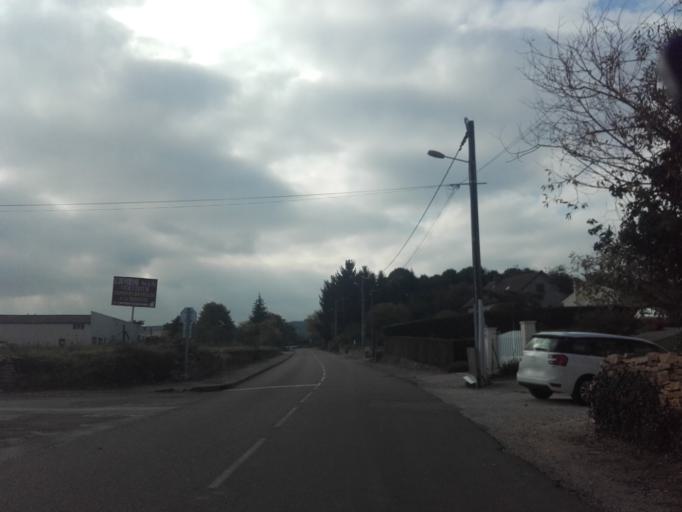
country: FR
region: Bourgogne
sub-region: Departement de Saone-et-Loire
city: Rully
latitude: 46.8797
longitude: 4.7552
